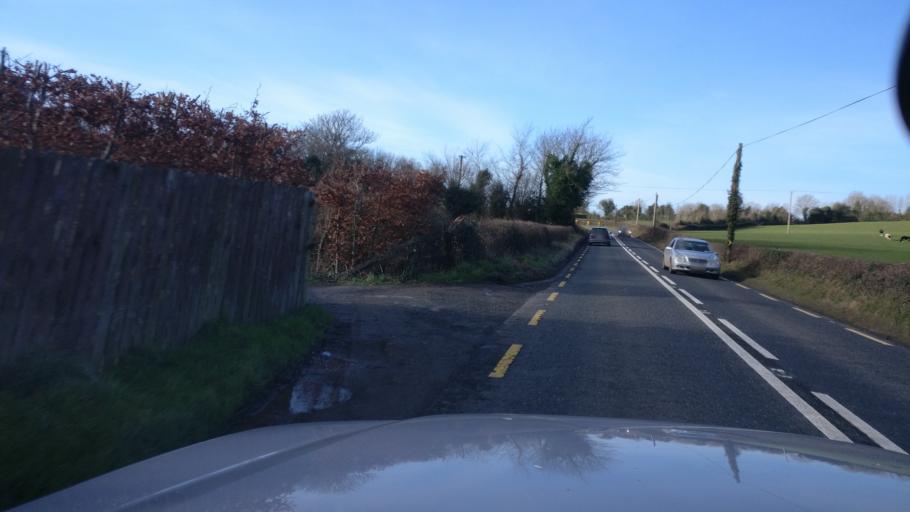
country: IE
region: Leinster
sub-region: Uibh Fhaili
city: Tullamore
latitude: 53.1963
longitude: -7.4168
